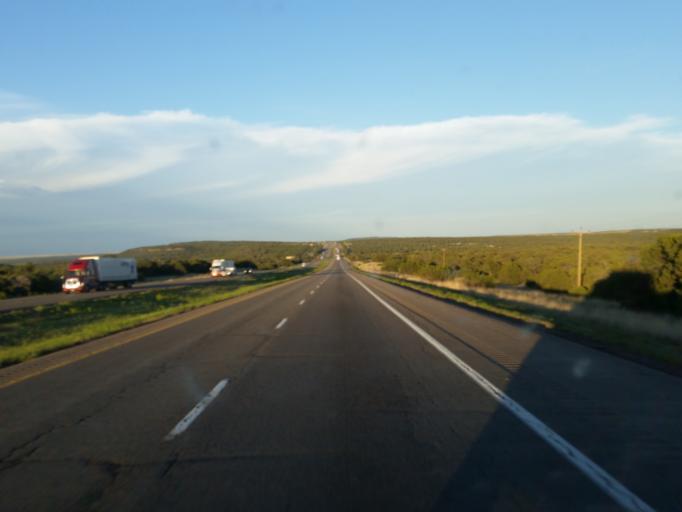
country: US
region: New Mexico
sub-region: Torrance County
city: Moriarty
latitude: 35.0038
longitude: -105.5878
